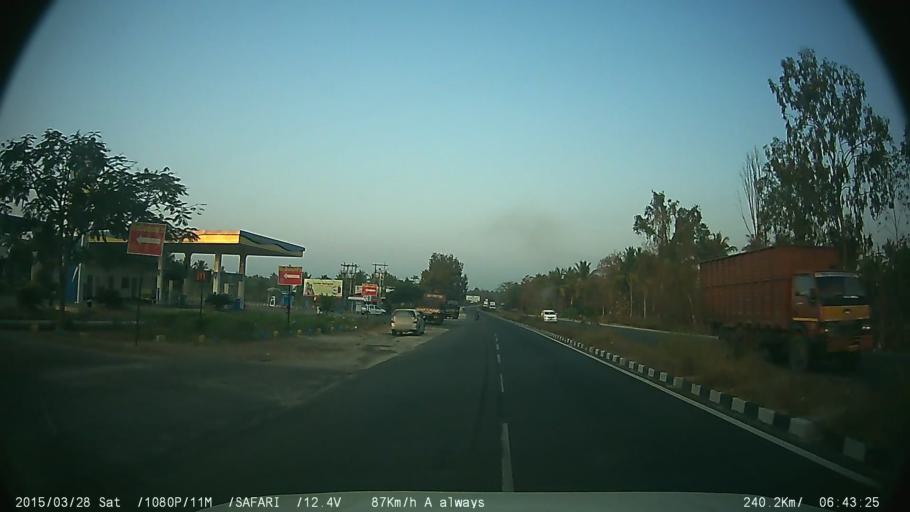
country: IN
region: Karnataka
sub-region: Ramanagara
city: Channapatna
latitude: 12.6326
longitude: 77.1188
